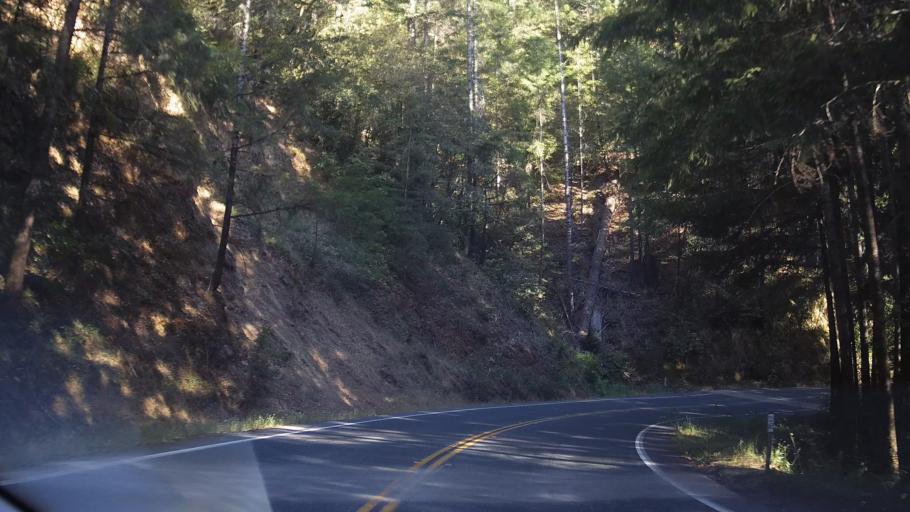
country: US
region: California
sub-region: Mendocino County
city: Brooktrails
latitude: 39.3665
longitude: -123.4987
